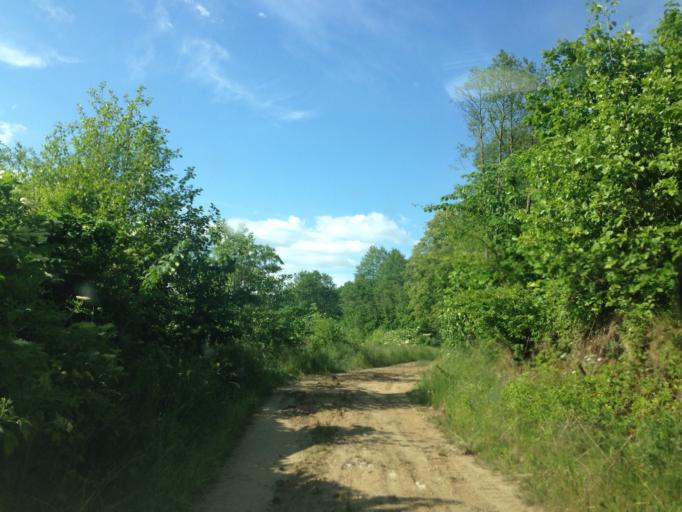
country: PL
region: Kujawsko-Pomorskie
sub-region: Powiat brodnicki
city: Brzozie
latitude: 53.3148
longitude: 19.5673
